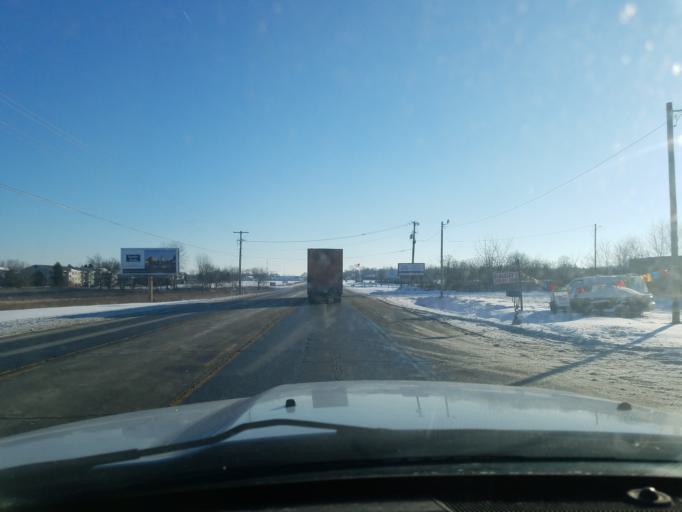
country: US
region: Indiana
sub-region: Noble County
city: Kendallville
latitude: 41.4524
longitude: -85.3004
